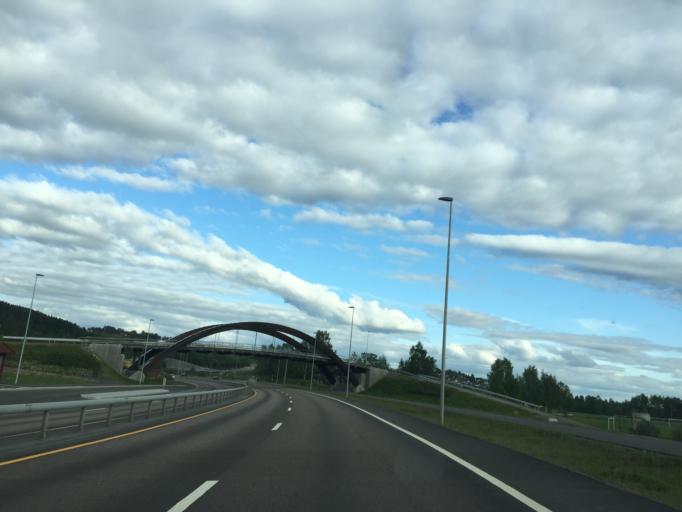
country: NO
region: Akershus
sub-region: Fet
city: Fetsund
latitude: 59.9420
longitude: 11.1167
